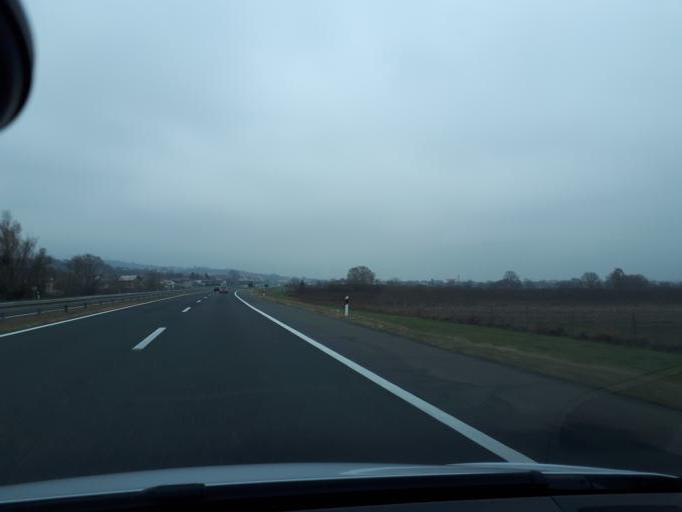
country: HR
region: Brodsko-Posavska
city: Slobodnica
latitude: 45.1765
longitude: 17.9622
